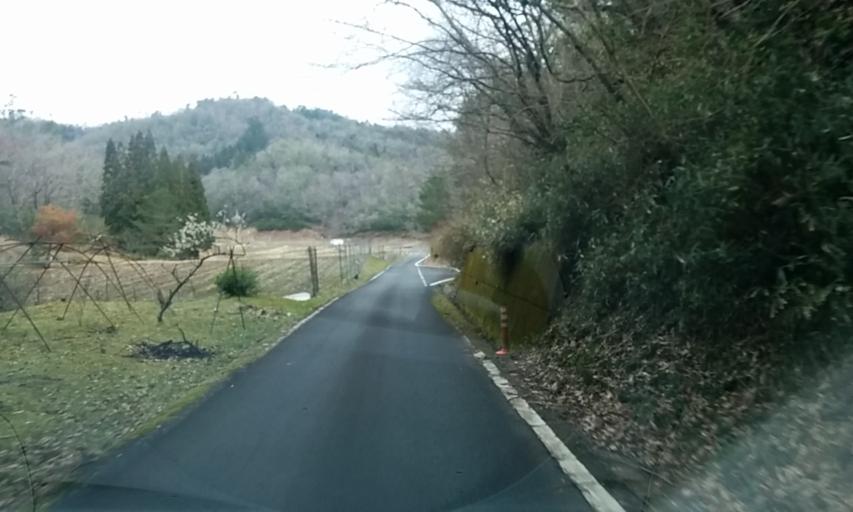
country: JP
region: Kyoto
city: Kameoka
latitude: 35.1144
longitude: 135.4258
